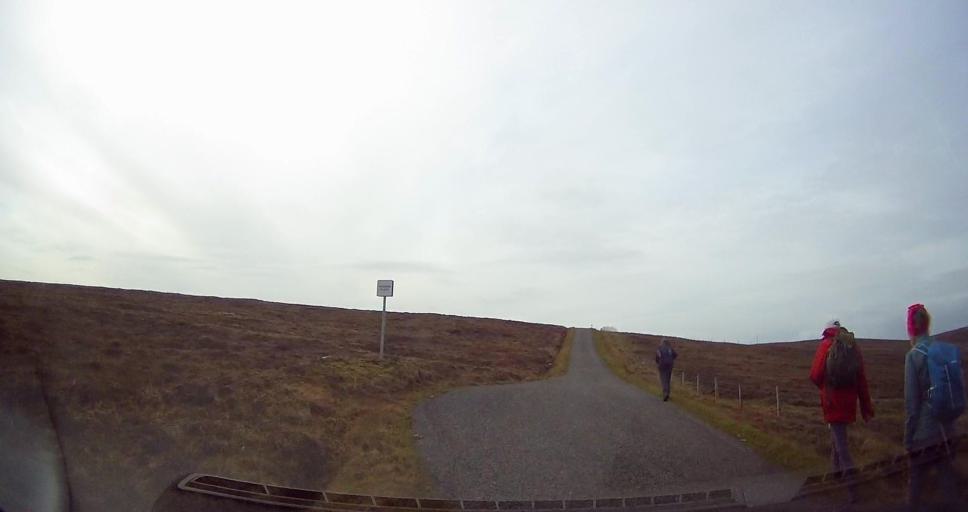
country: GB
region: Scotland
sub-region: Shetland Islands
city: Shetland
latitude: 60.1516
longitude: -1.0875
